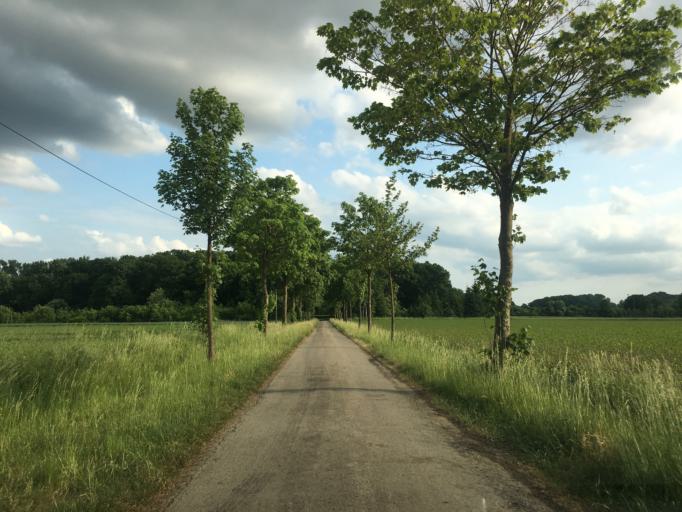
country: DE
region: North Rhine-Westphalia
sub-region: Regierungsbezirk Munster
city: Altenberge
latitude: 52.0271
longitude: 7.5401
